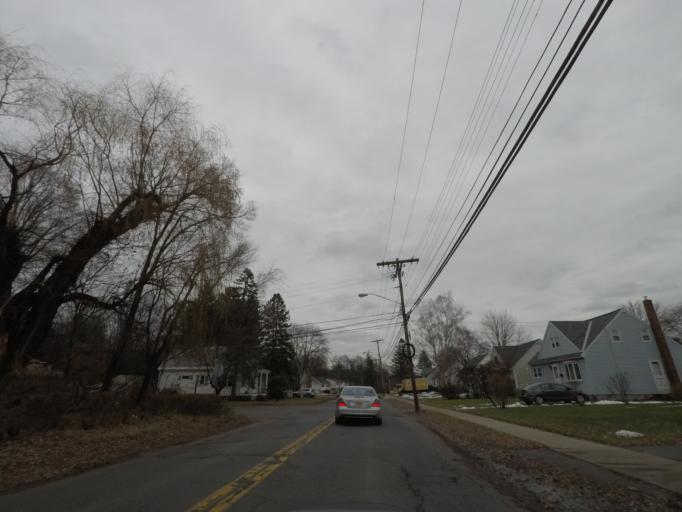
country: US
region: New York
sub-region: Schenectady County
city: Schenectady
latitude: 42.7876
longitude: -73.9052
